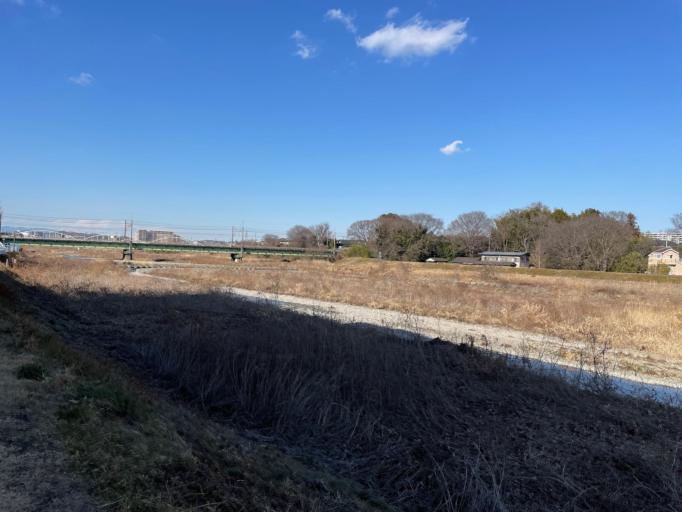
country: JP
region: Tokyo
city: Hachioji
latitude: 35.6492
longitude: 139.3615
